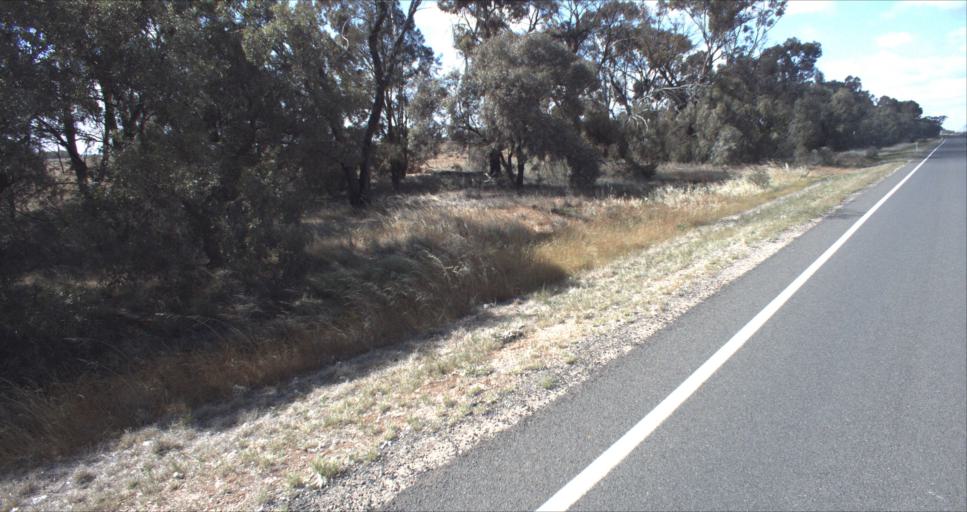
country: AU
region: New South Wales
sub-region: Murrumbidgee Shire
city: Darlington Point
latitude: -34.5339
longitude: 146.1734
